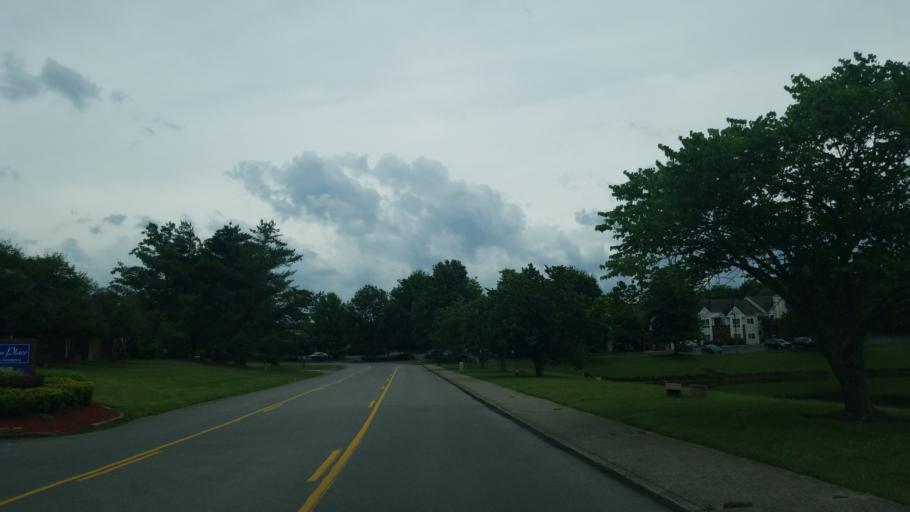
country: US
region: Tennessee
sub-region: Williamson County
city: Brentwood
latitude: 36.0318
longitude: -86.8018
